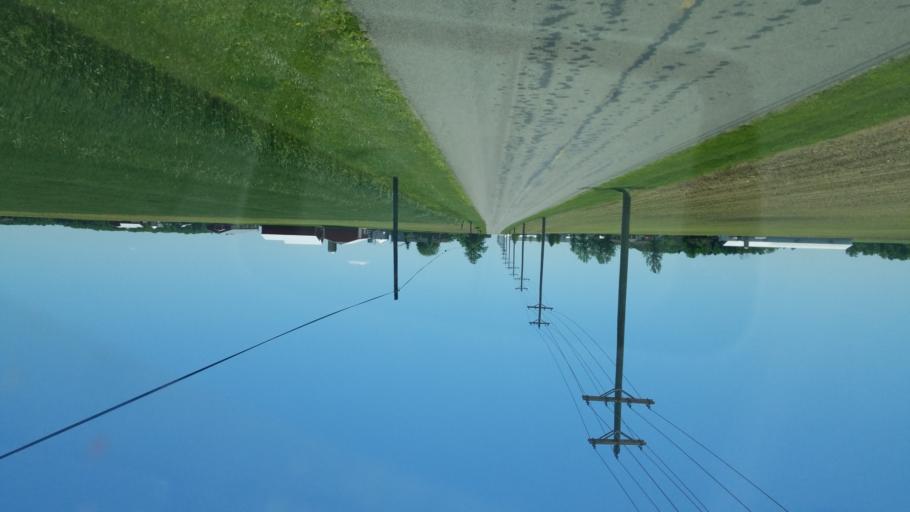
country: US
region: Ohio
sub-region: Mercer County
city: Fort Recovery
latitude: 40.3751
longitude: -84.7290
